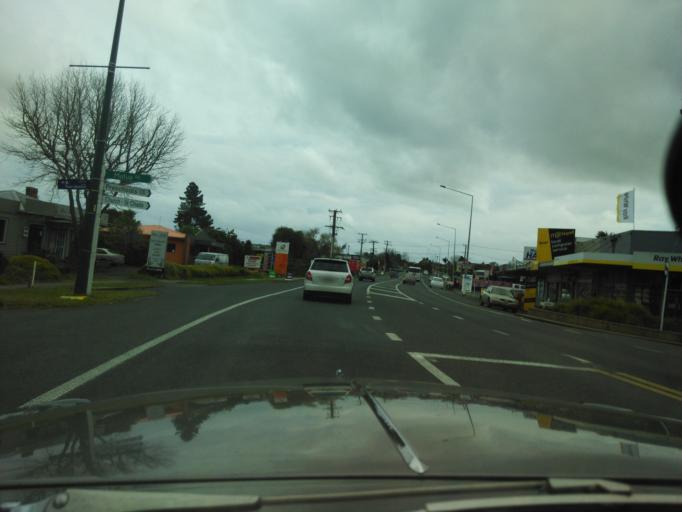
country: NZ
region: Auckland
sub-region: Auckland
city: Muriwai Beach
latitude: -36.7725
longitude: 174.5466
